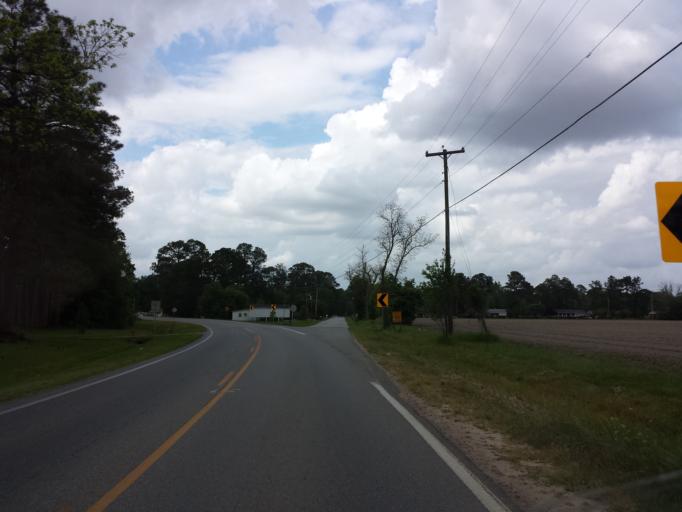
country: US
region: Georgia
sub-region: Cook County
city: Adel
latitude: 31.1196
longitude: -83.4154
